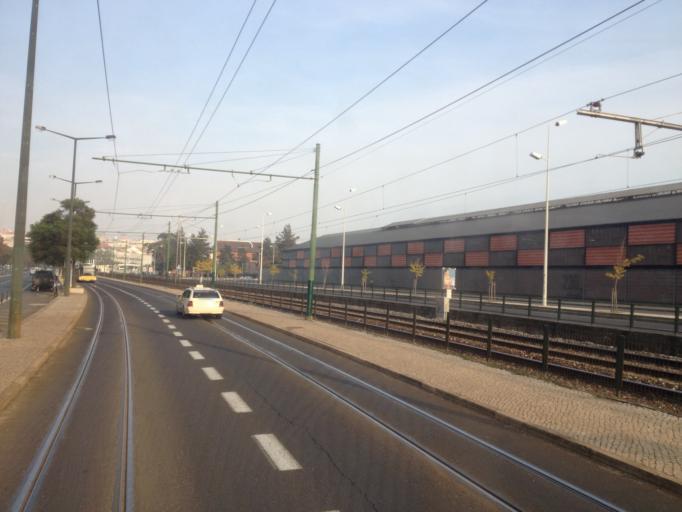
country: PT
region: Setubal
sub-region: Almada
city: Cacilhas
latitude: 38.7044
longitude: -9.1599
